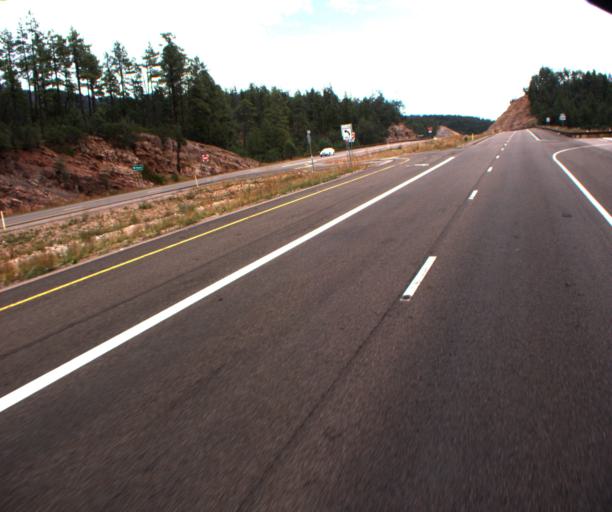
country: US
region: Arizona
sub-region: Gila County
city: Star Valley
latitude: 34.3239
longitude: -111.0813
